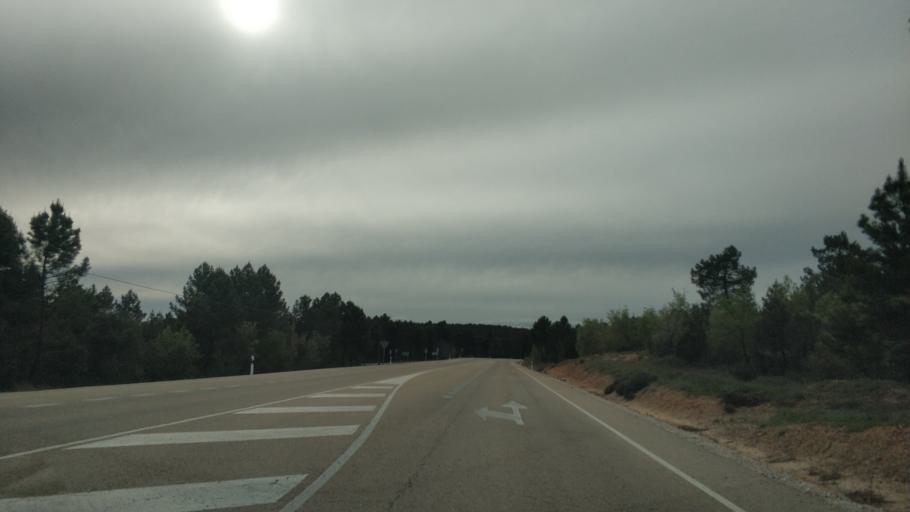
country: ES
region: Castille and Leon
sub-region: Provincia de Soria
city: Bayubas de Abajo
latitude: 41.5111
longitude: -2.9217
